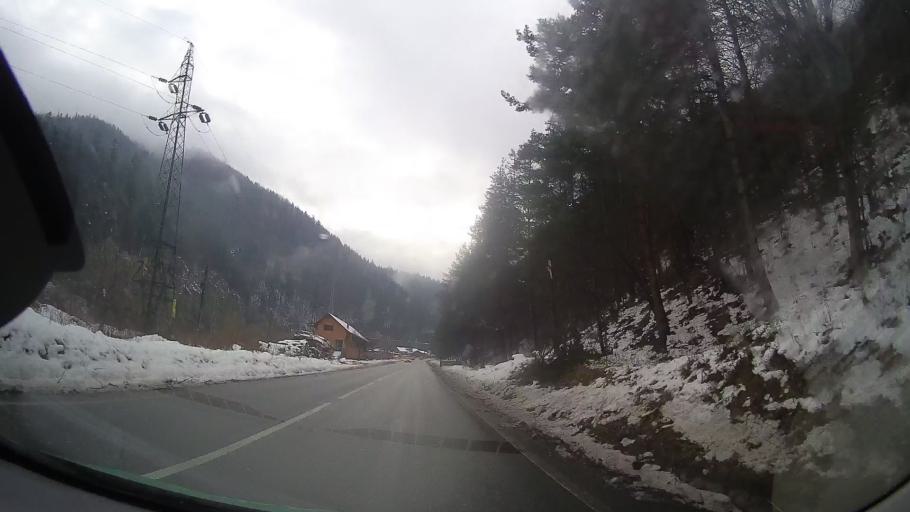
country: RO
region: Neamt
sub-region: Comuna Bicaz
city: Bicaz
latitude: 46.8983
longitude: 26.0549
